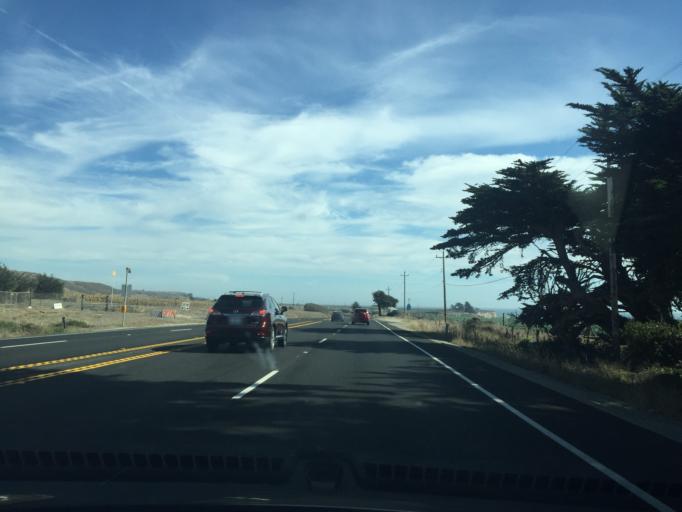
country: US
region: California
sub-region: Santa Cruz County
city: Bonny Doon
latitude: 36.9734
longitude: -122.1288
